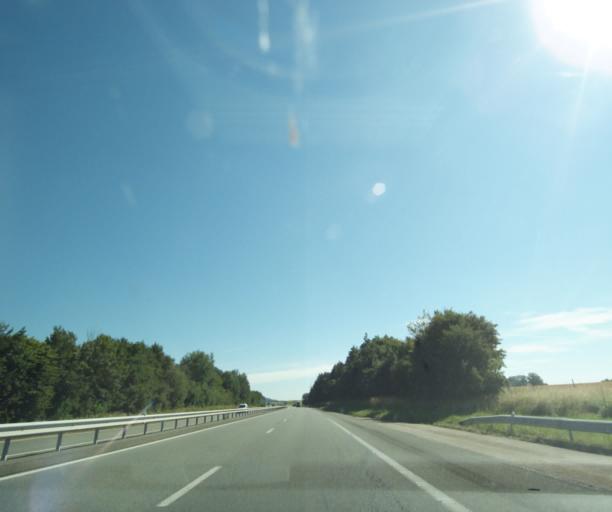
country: FR
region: Champagne-Ardenne
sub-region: Departement de la Haute-Marne
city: Avrecourt
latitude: 48.0250
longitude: 5.5397
